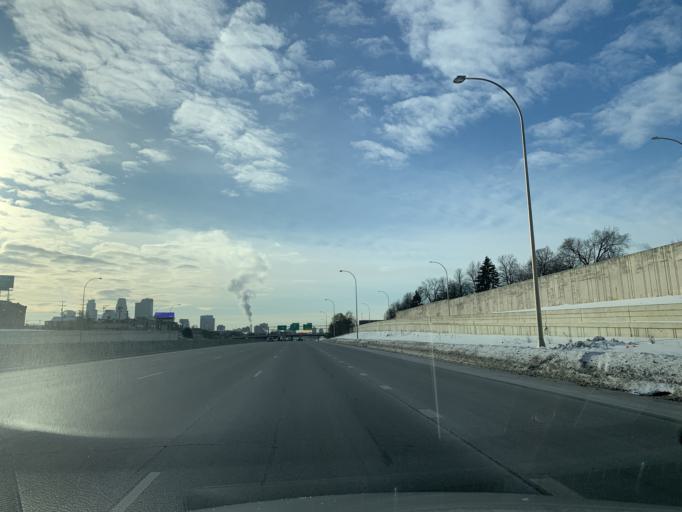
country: US
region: Minnesota
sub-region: Hennepin County
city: Minneapolis
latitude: 45.0042
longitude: -93.2829
